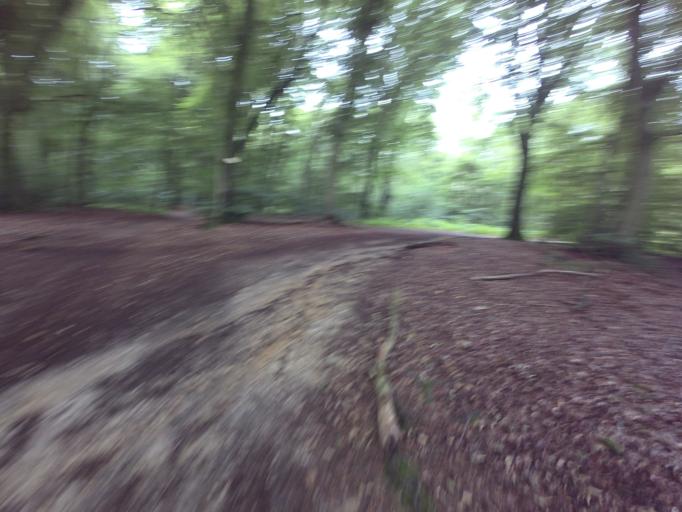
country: BE
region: Wallonia
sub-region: Province de Liege
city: Plombieres
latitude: 50.7692
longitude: 5.9712
